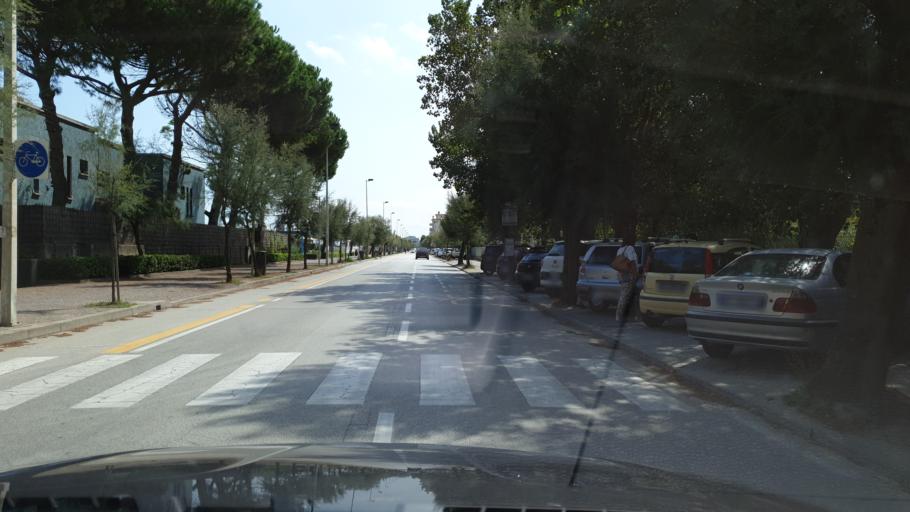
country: IT
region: Emilia-Romagna
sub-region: Provincia di Rimini
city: Misano Adriatico
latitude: 43.9884
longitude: 12.6838
